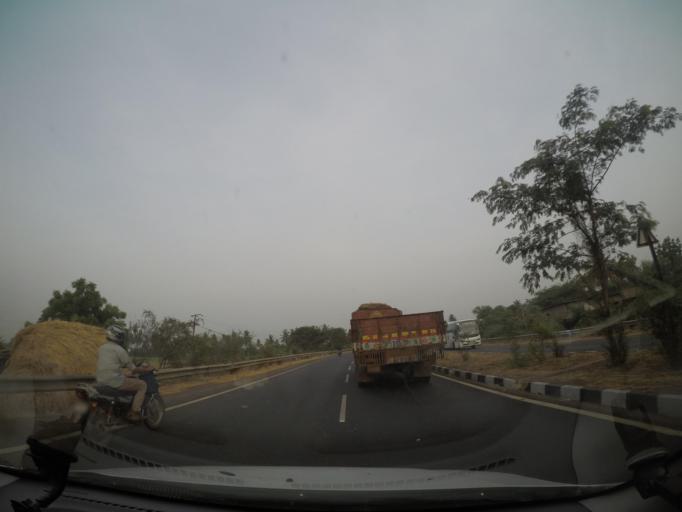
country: IN
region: Andhra Pradesh
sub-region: Krishna
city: Gannavaram
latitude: 16.6093
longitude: 80.9186
